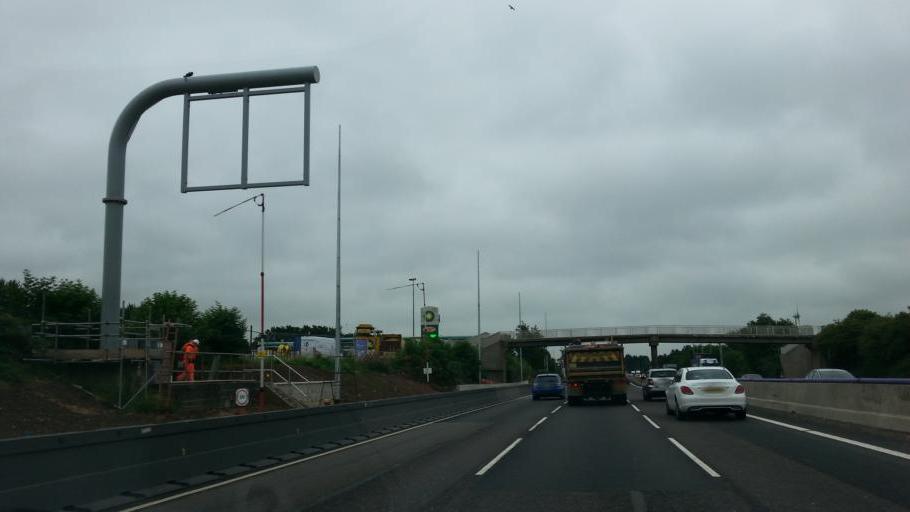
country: GB
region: England
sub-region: Northamptonshire
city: Long Buckby
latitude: 52.3079
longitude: -1.1227
